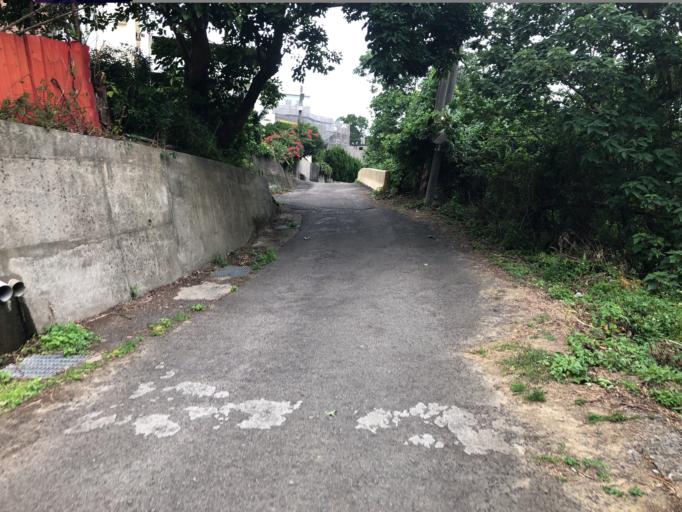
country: TW
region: Taiwan
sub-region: Hsinchu
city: Hsinchu
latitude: 24.7552
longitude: 120.9474
